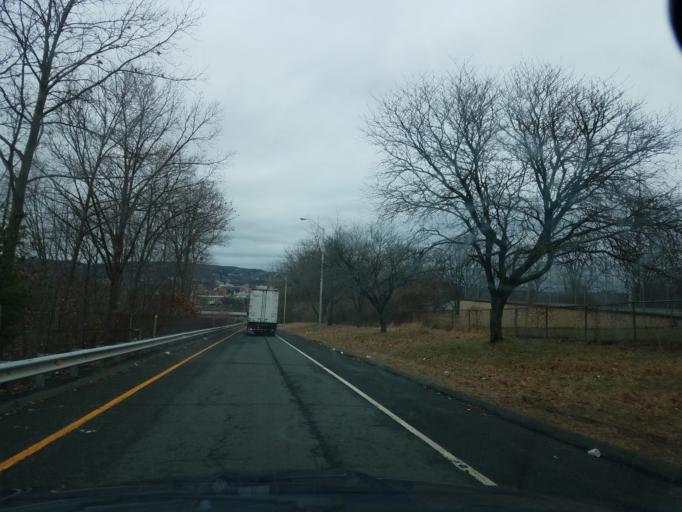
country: US
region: Connecticut
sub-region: New Haven County
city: Waterbury
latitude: 41.5503
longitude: -73.0569
